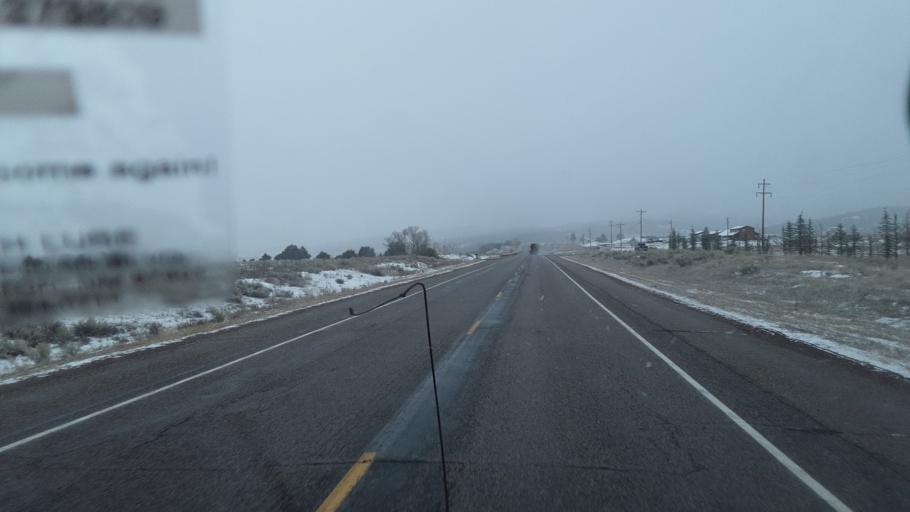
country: US
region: New Mexico
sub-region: Rio Arriba County
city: Tierra Amarilla
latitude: 36.7701
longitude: -106.5564
